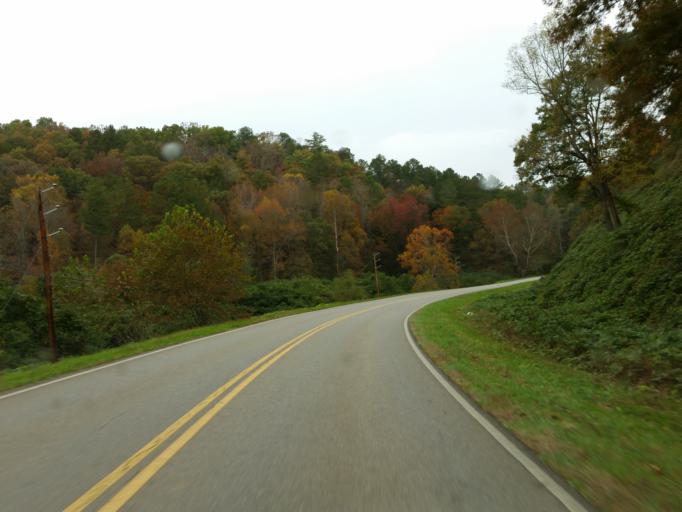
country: US
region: Georgia
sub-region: Pickens County
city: Jasper
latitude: 34.4819
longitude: -84.4235
